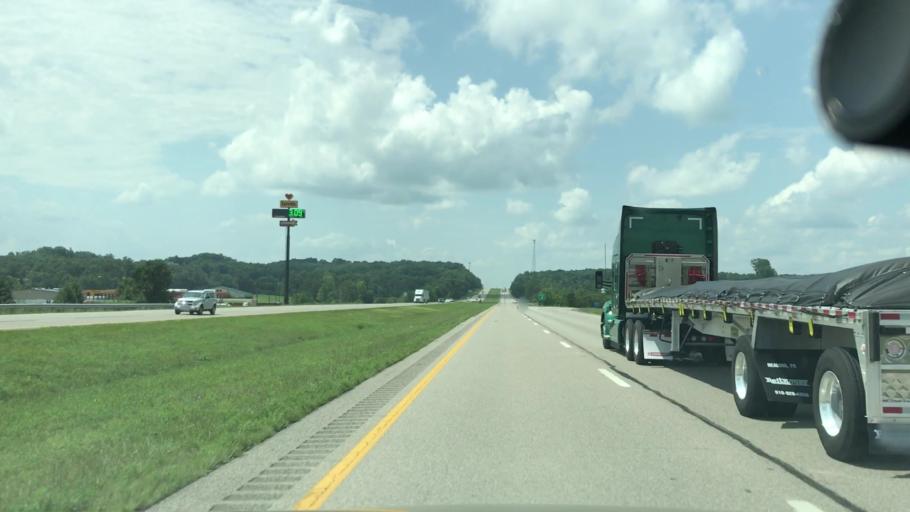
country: US
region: Ohio
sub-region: Gallia County
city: Gallipolis
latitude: 38.8765
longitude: -82.2921
